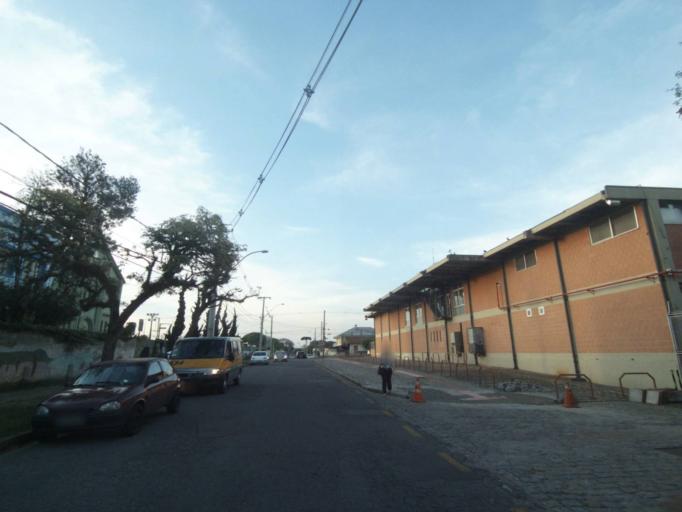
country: BR
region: Parana
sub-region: Curitiba
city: Curitiba
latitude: -25.4633
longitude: -49.3077
